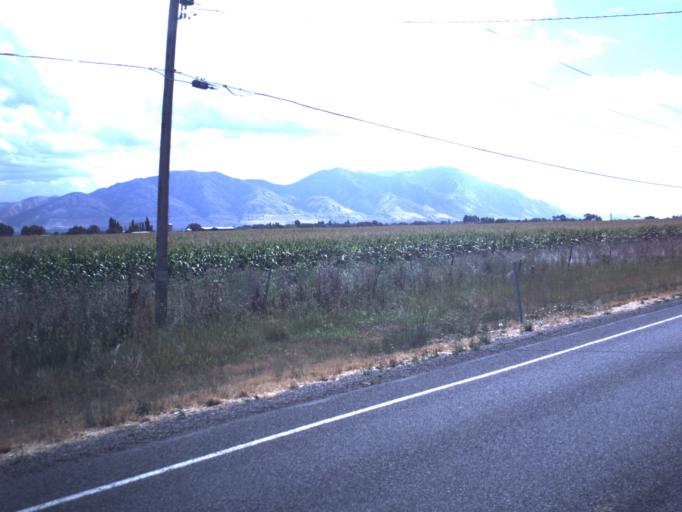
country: US
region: Utah
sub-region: Box Elder County
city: Honeyville
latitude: 41.5708
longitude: -112.1297
